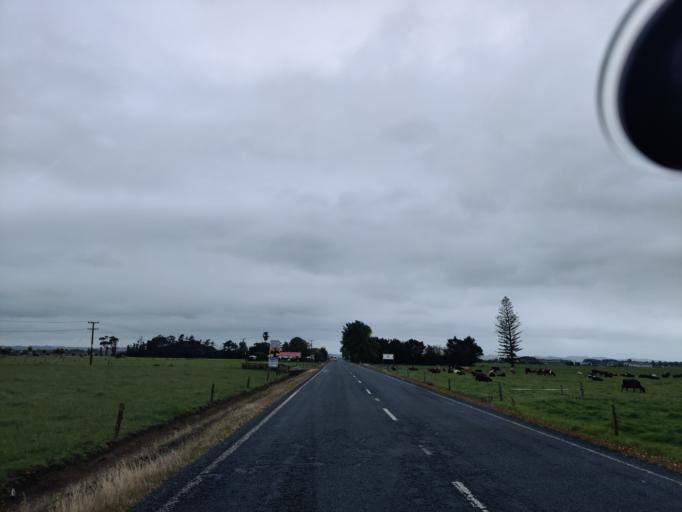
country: NZ
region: Northland
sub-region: Kaipara District
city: Dargaville
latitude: -36.1219
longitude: 174.0045
